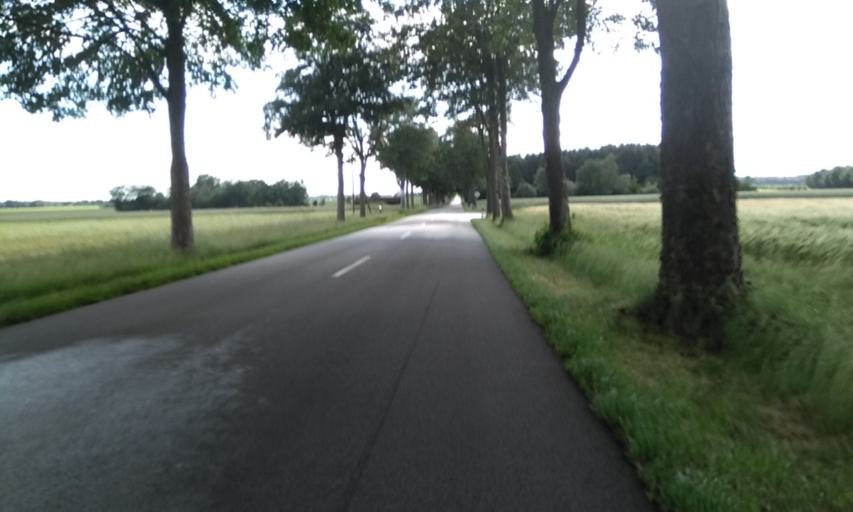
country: DE
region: Lower Saxony
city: Vierden
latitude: 53.3565
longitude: 9.5025
